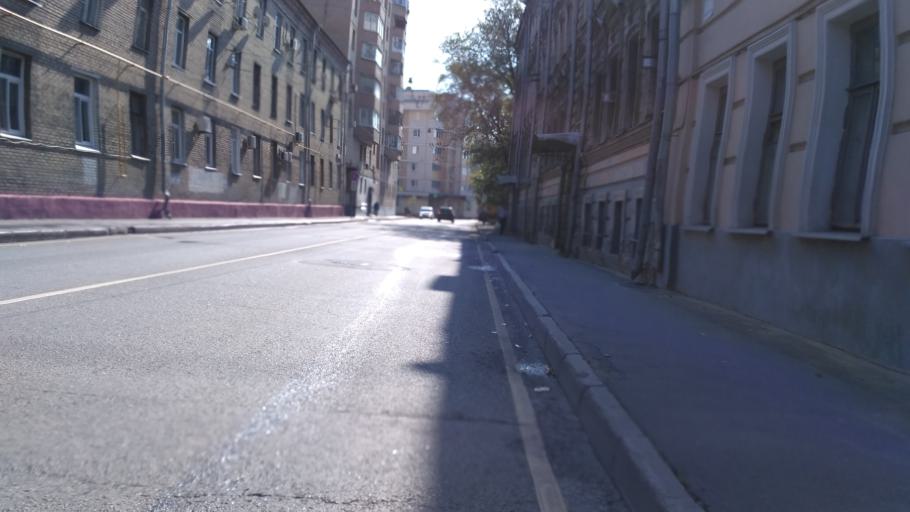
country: RU
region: Moscow
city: Lefortovo
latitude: 55.7676
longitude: 37.6734
